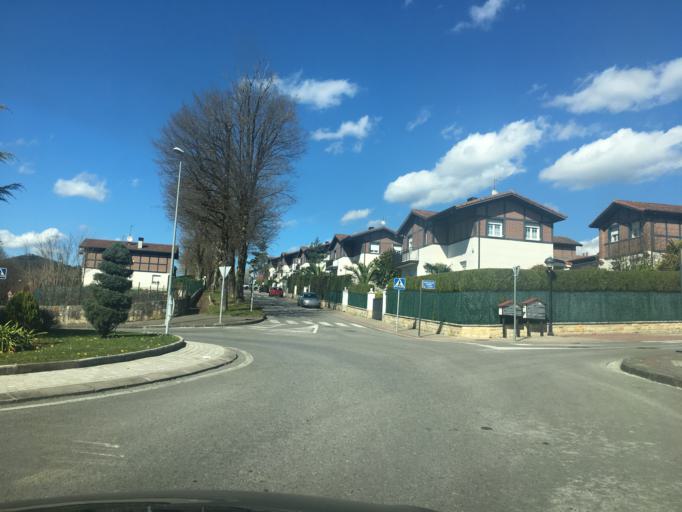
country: ES
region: Basque Country
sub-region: Bizkaia
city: Amorebieta
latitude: 43.2305
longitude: -2.7386
